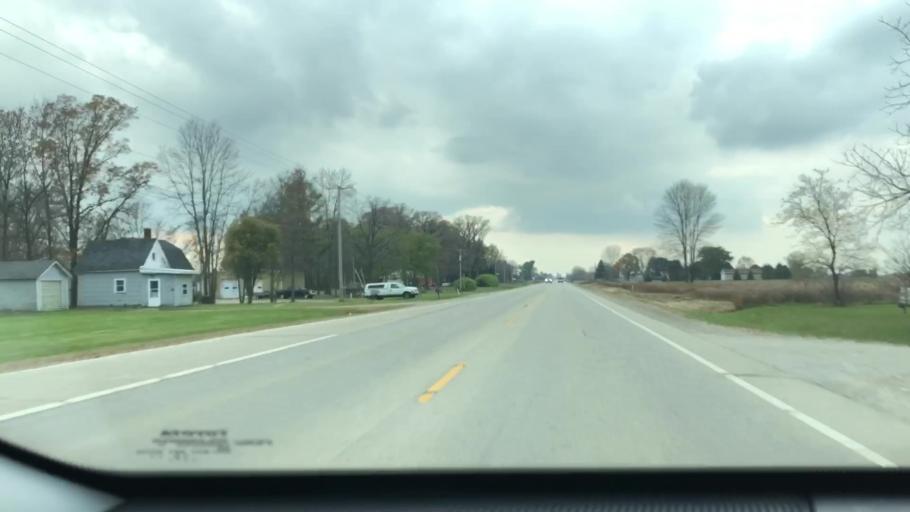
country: US
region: Wisconsin
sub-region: Outagamie County
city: Seymour
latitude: 44.5013
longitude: -88.2716
